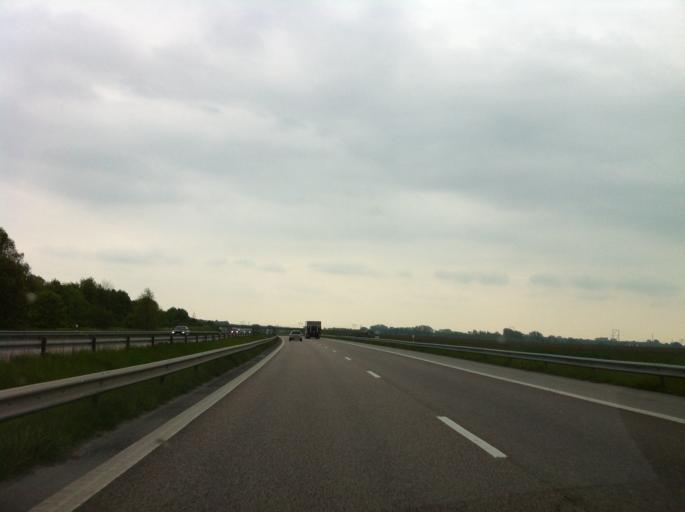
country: SE
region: Skane
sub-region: Kavlinge Kommun
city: Loddekopinge
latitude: 55.7547
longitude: 12.9999
